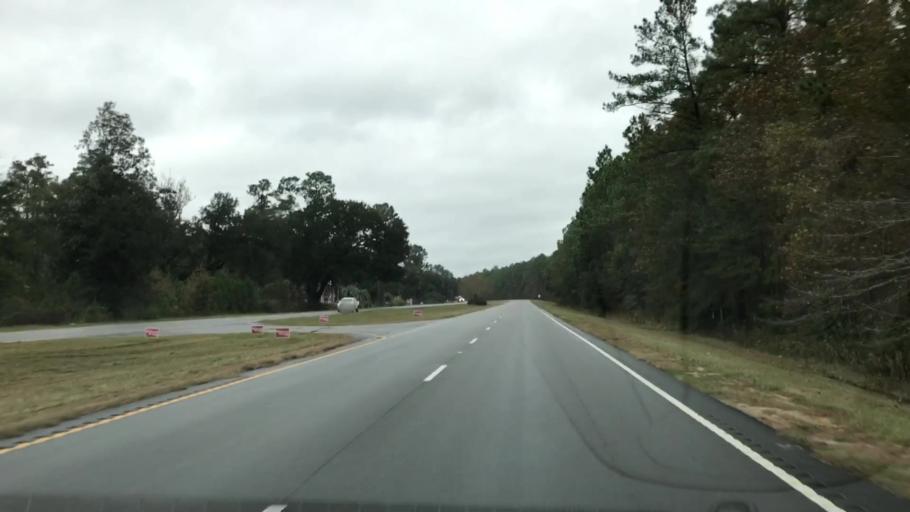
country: US
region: South Carolina
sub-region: Georgetown County
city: Georgetown
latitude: 33.2279
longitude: -79.3770
